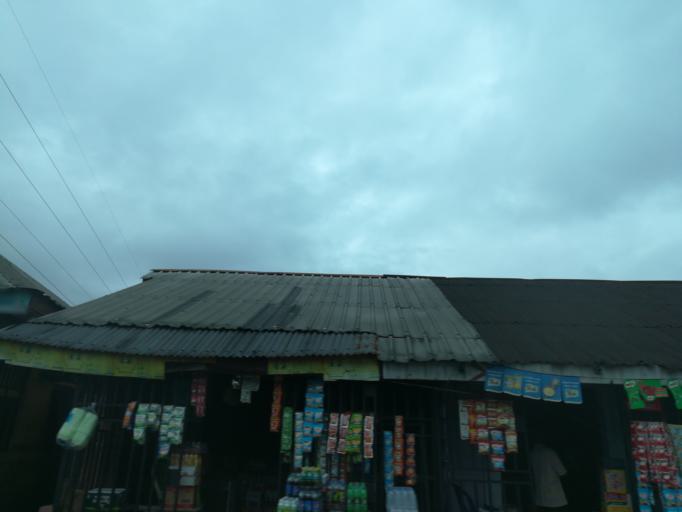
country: NG
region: Rivers
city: Port Harcourt
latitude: 4.8123
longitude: 7.0185
